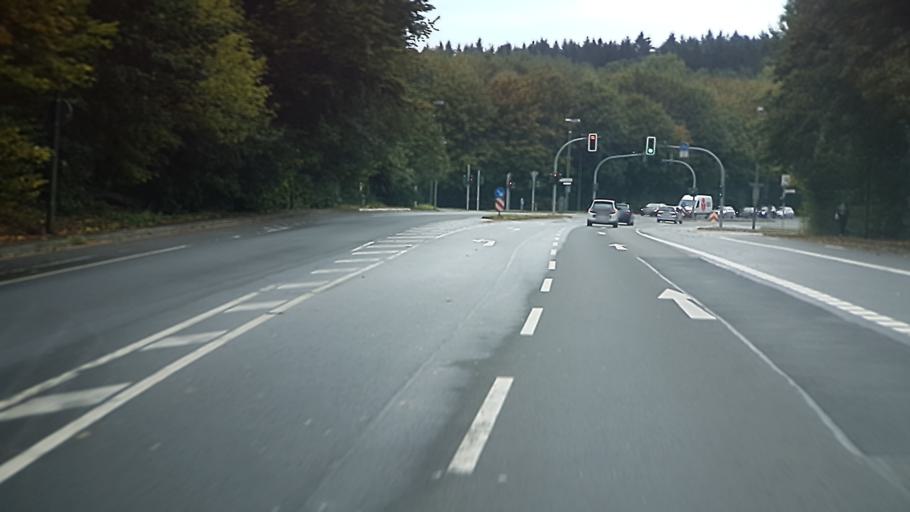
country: DE
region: North Rhine-Westphalia
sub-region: Regierungsbezirk Arnsberg
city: Luedenscheid
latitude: 51.2031
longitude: 7.6552
